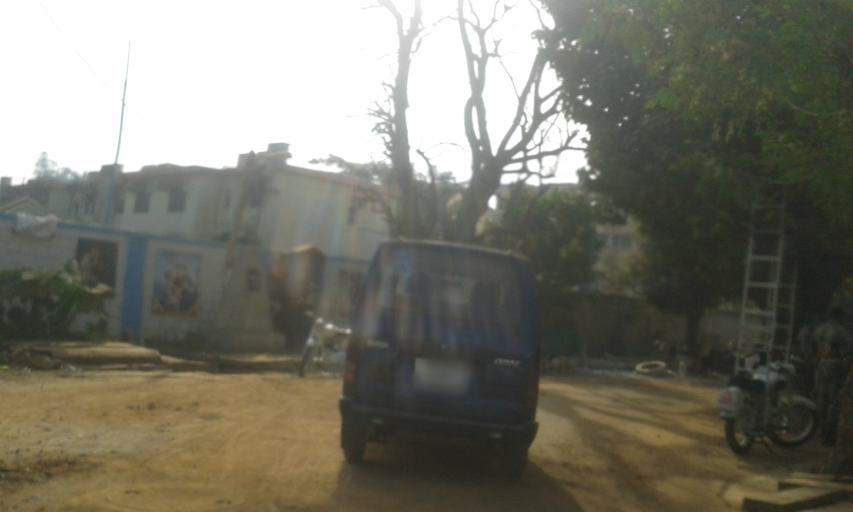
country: IN
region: Karnataka
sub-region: Bangalore Urban
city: Bangalore
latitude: 12.9609
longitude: 77.6182
